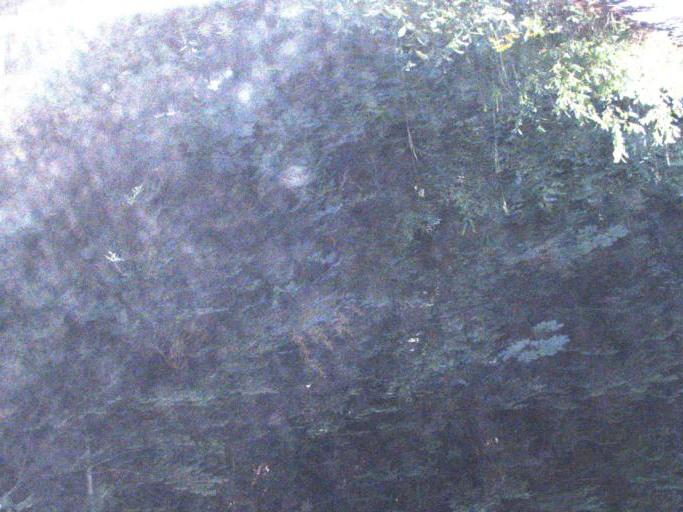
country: US
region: Washington
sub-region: King County
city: Enumclaw
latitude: 46.8319
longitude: -121.5247
